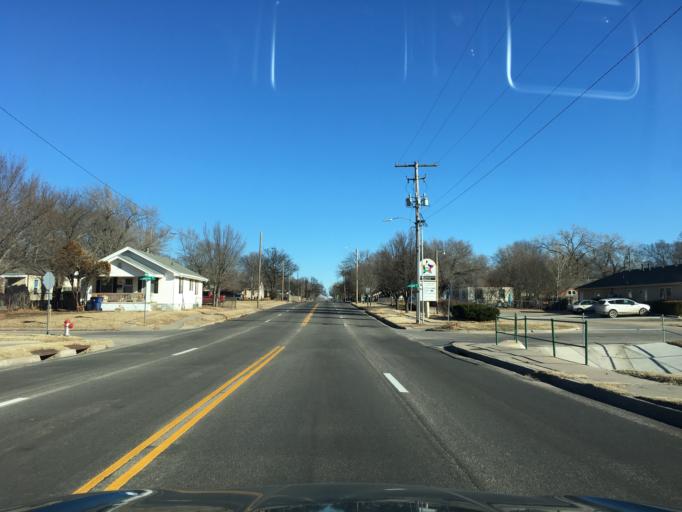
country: US
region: Kansas
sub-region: Sedgwick County
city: Wichita
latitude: 37.6719
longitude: -97.2879
